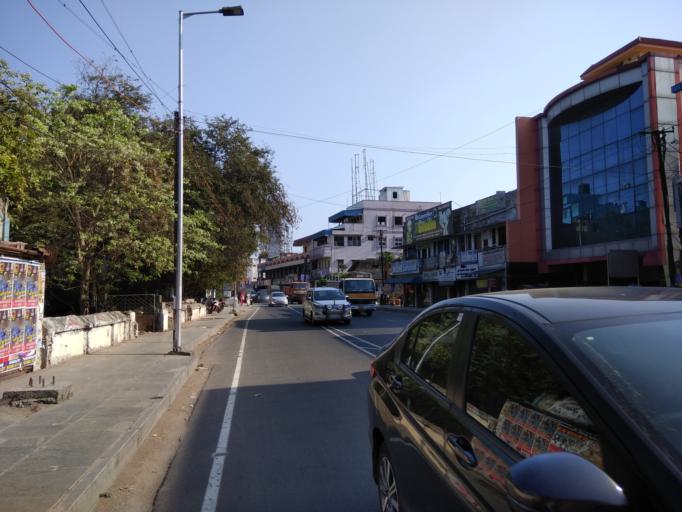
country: IN
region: Tamil Nadu
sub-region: Kancheepuram
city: Saint Thomas Mount
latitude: 13.0084
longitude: 80.1963
